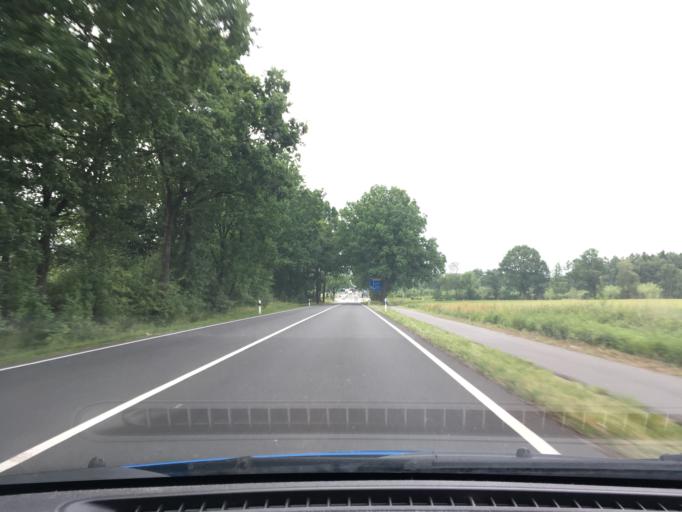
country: DE
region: Lower Saxony
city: Wenzendorf
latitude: 53.3666
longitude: 9.8057
